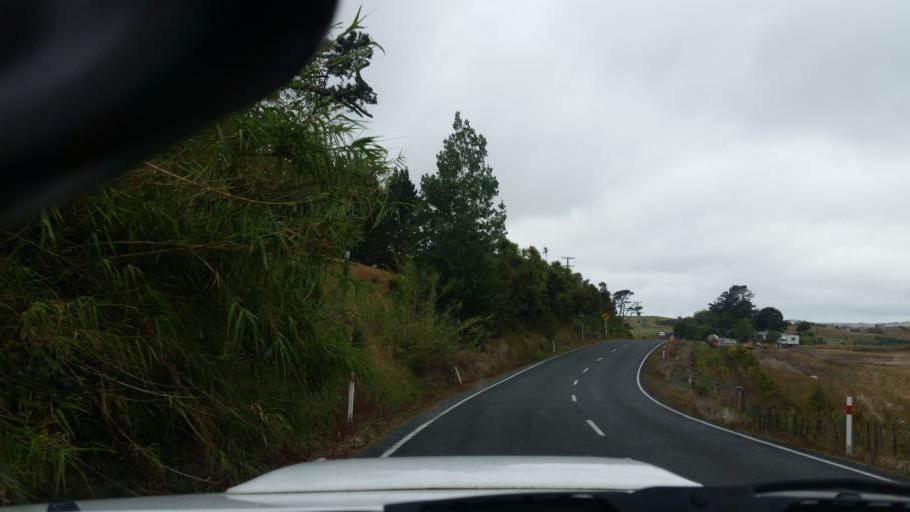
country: NZ
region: Auckland
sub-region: Auckland
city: Wellsford
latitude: -36.1439
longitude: 174.4862
